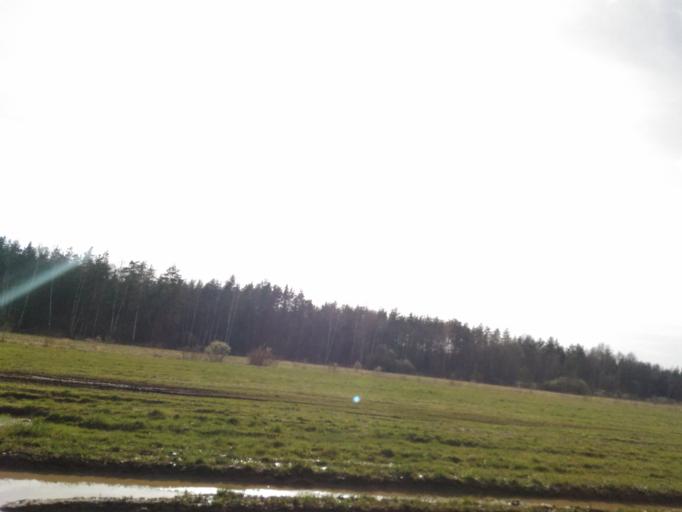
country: RU
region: Vladimir
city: Petushki
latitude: 55.8893
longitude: 39.4940
